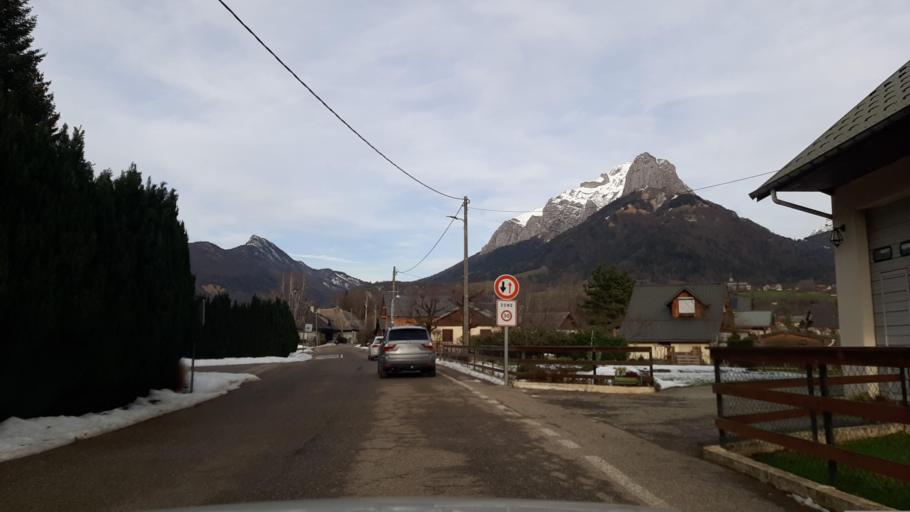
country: FR
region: Rhone-Alpes
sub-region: Departement de la Savoie
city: Gresy-sur-Isere
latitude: 45.6463
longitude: 6.1654
